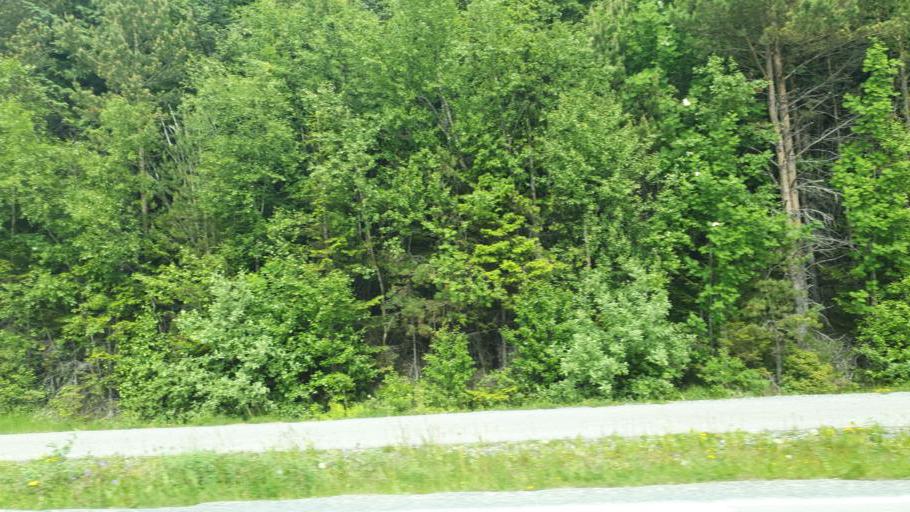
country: NO
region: Sor-Trondelag
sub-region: Trondheim
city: Trondheim
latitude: 63.5697
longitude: 10.4119
